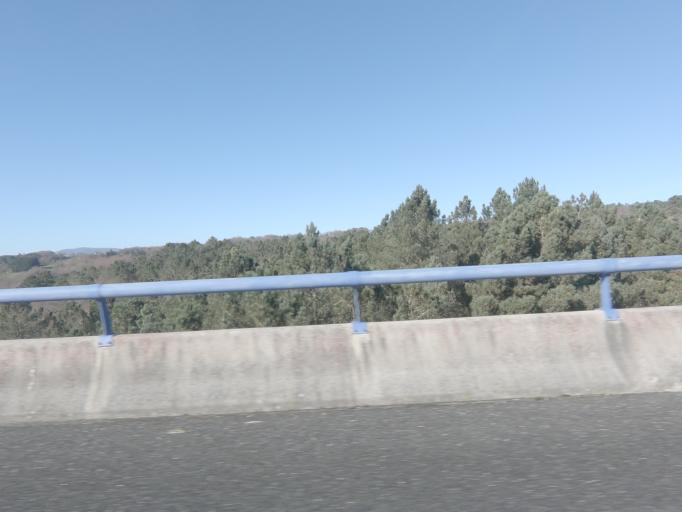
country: ES
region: Galicia
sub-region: Provincia de Pontevedra
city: Lalin
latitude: 42.6149
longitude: -8.0987
